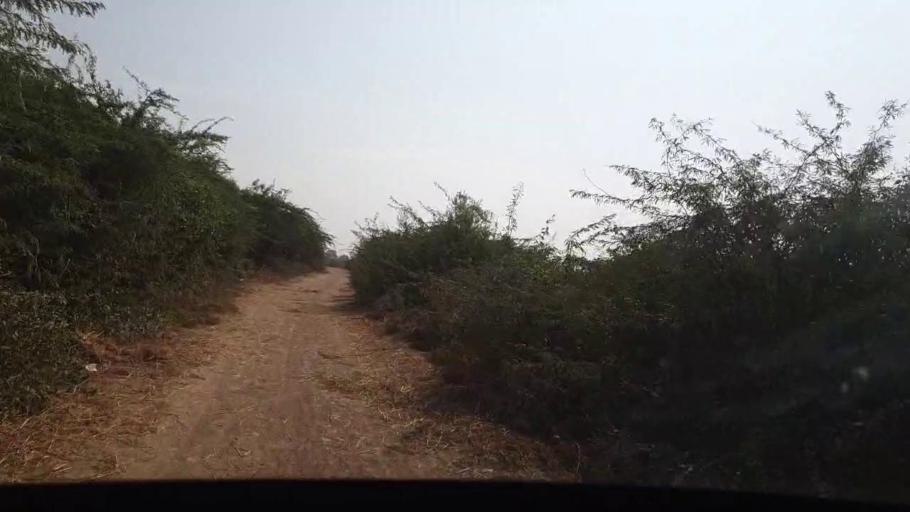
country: PK
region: Sindh
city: Chuhar Jamali
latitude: 24.2684
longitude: 67.9237
